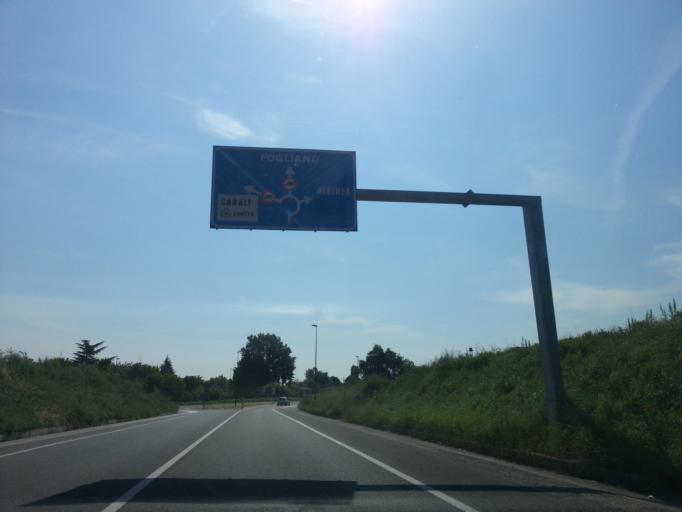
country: IT
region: Emilia-Romagna
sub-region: Provincia di Reggio Emilia
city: Albinea
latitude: 44.6575
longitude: 10.6110
